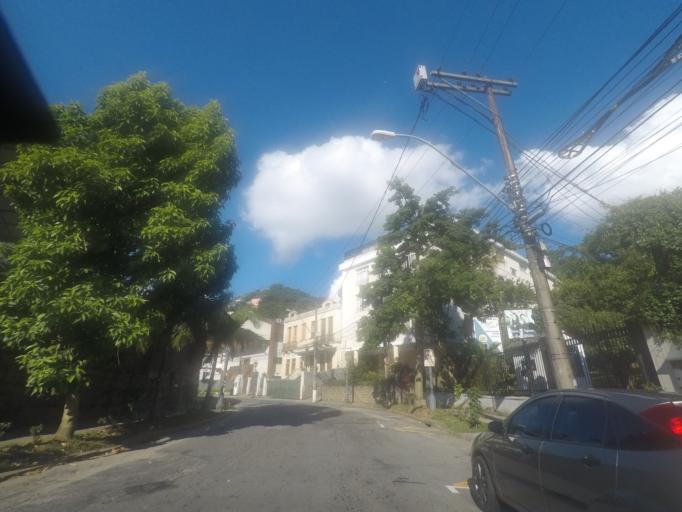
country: BR
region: Rio de Janeiro
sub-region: Petropolis
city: Petropolis
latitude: -22.5074
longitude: -43.1668
